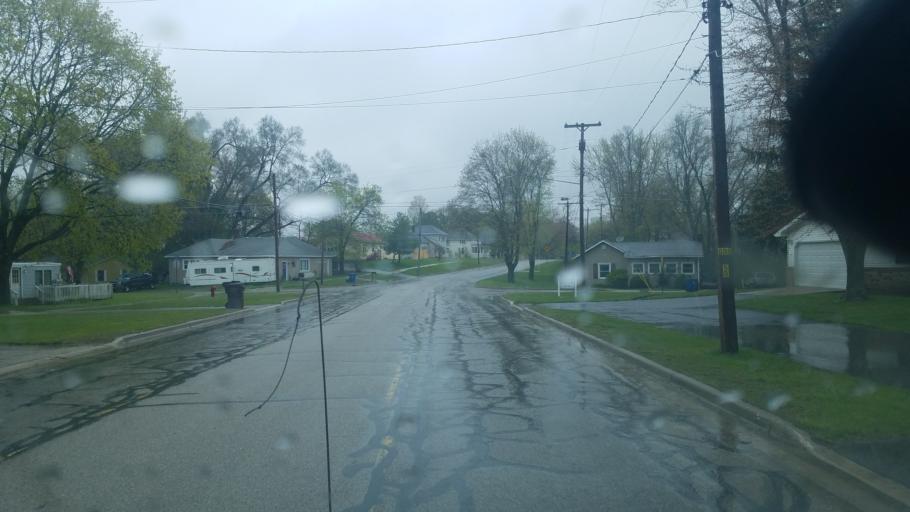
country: US
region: Michigan
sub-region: Montcalm County
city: Lakeview
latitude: 43.4455
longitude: -85.2820
